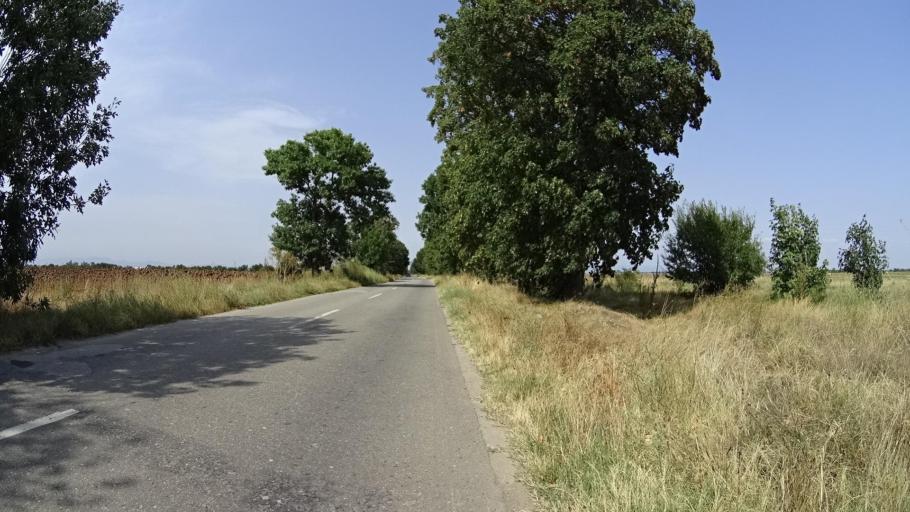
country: BG
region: Plovdiv
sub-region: Obshtina Plovdiv
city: Plovdiv
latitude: 42.2545
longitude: 24.7987
